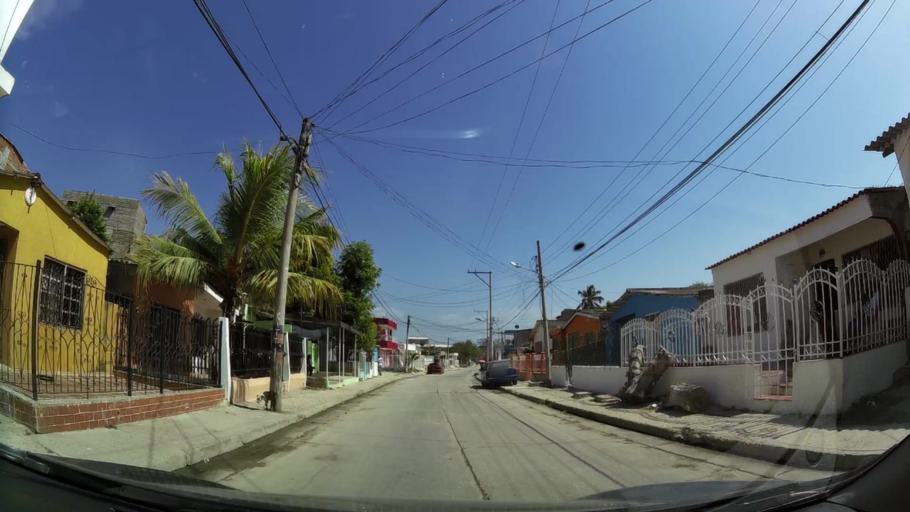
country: CO
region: Bolivar
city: Cartagena
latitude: 10.4357
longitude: -75.5203
